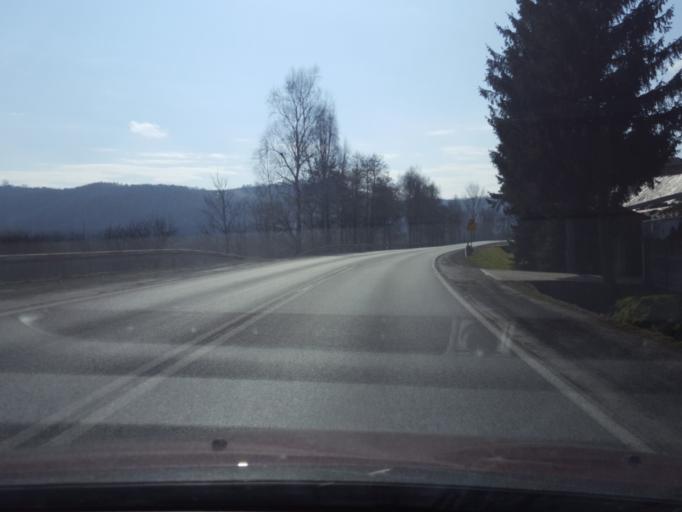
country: PL
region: Lesser Poland Voivodeship
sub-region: Powiat nowosadecki
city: Lososina Dolna
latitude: 49.6995
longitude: 20.6594
